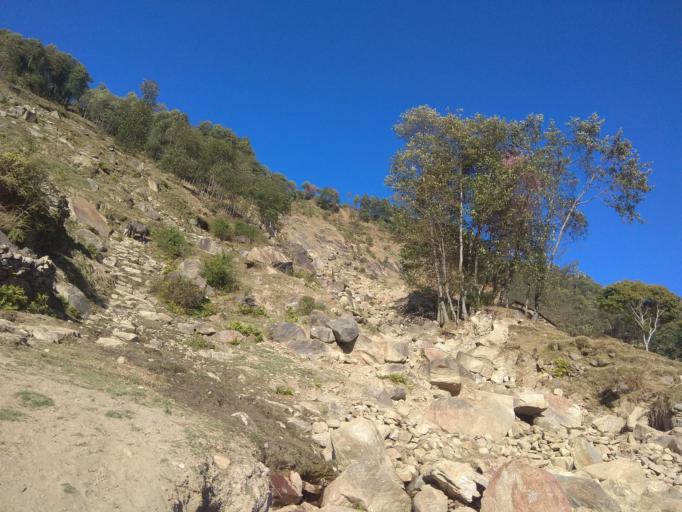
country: NP
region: Far Western
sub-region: Seti Zone
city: Achham
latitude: 29.2564
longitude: 81.6398
